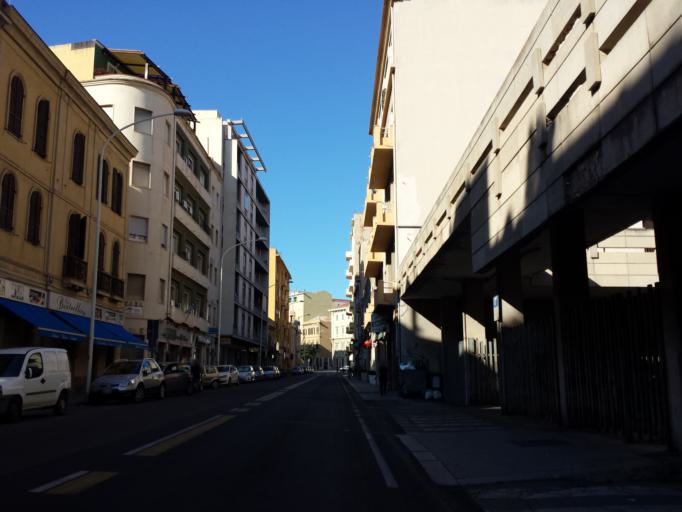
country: IT
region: Sardinia
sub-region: Provincia di Cagliari
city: Cagliari
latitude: 39.2127
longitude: 9.1179
